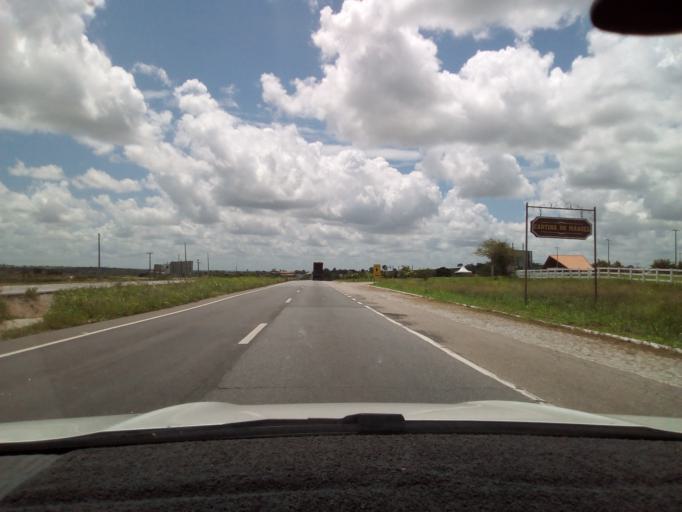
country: BR
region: Paraiba
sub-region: Gurinhem
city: Gurinhem
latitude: -7.1714
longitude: -35.3850
